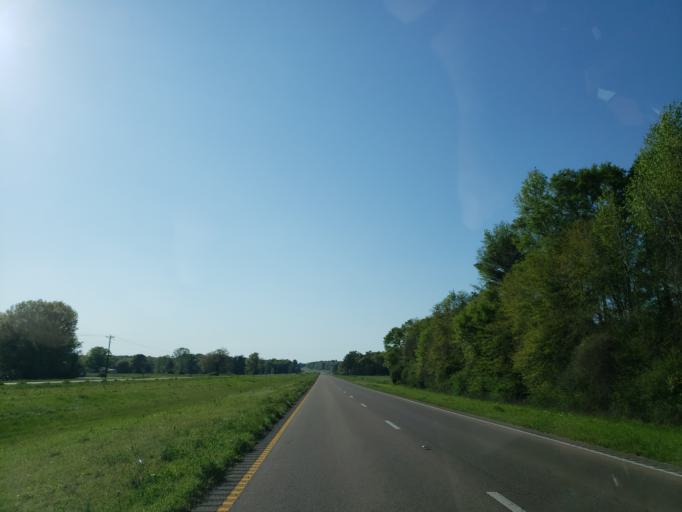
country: US
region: Mississippi
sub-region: Jones County
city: Ellisville
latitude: 31.6779
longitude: -89.3017
